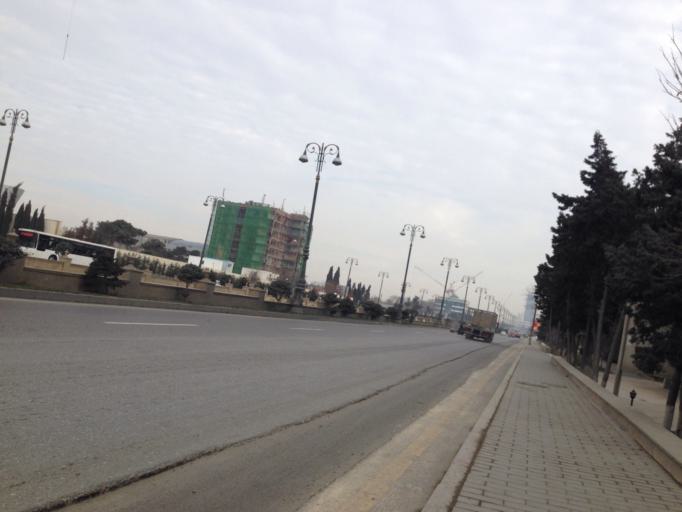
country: AZ
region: Baki
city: Baku
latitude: 40.4047
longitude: 49.8856
